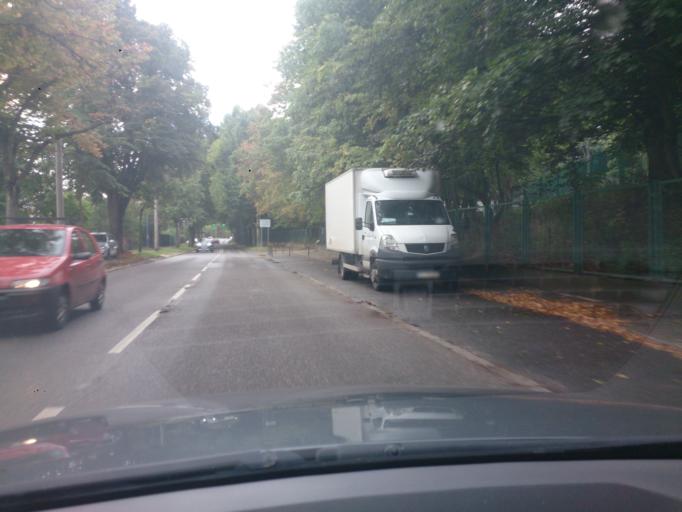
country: PL
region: Pomeranian Voivodeship
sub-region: Sopot
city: Sopot
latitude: 54.4000
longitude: 18.5626
